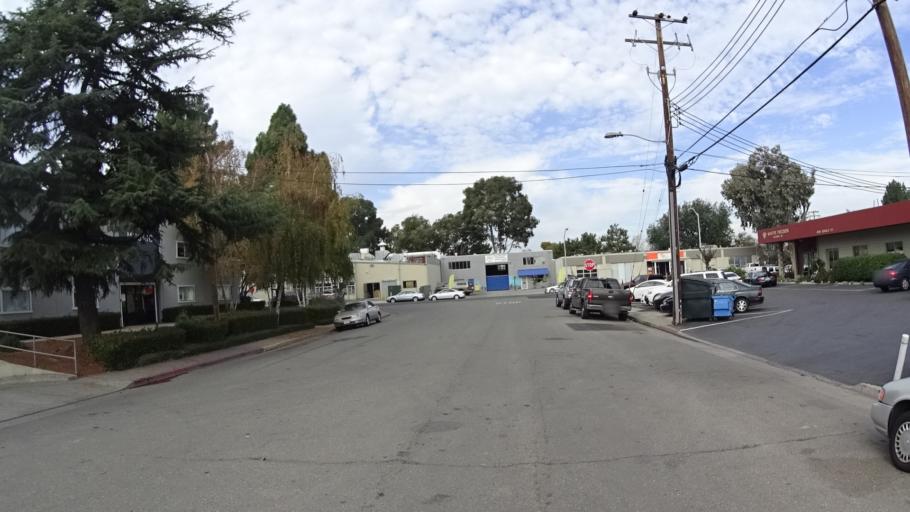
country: US
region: California
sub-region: Santa Clara County
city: Santa Clara
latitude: 37.3620
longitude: -121.9519
